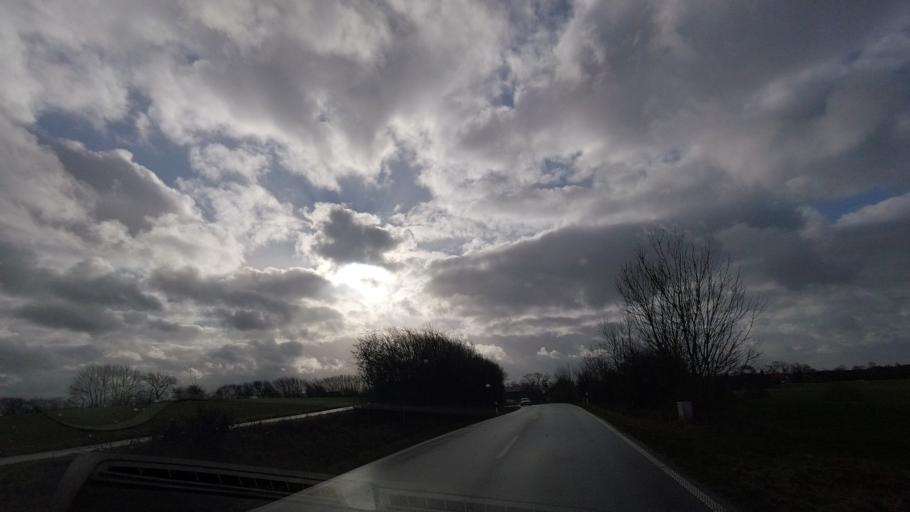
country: DE
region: Schleswig-Holstein
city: Grodersby
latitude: 54.6423
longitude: 9.9204
